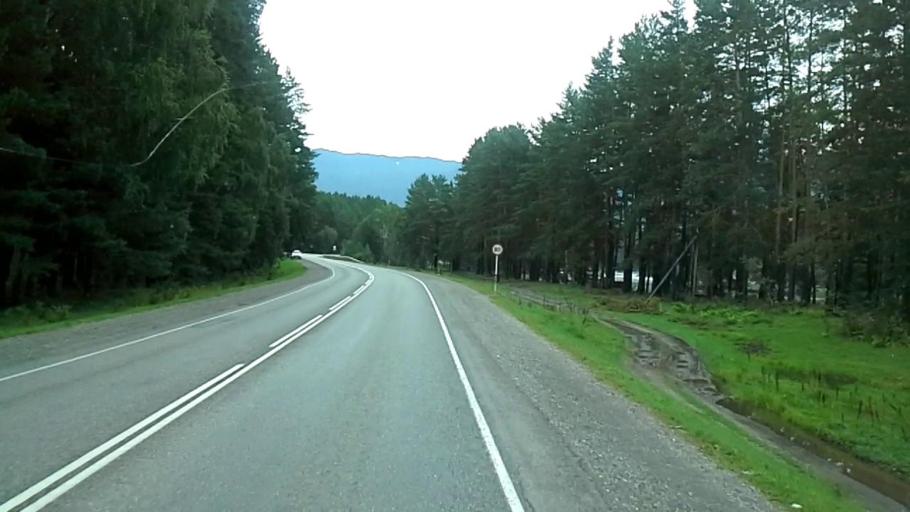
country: RU
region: Altay
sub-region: Mayminskiy Rayon
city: Manzherok
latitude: 51.8324
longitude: 85.7543
